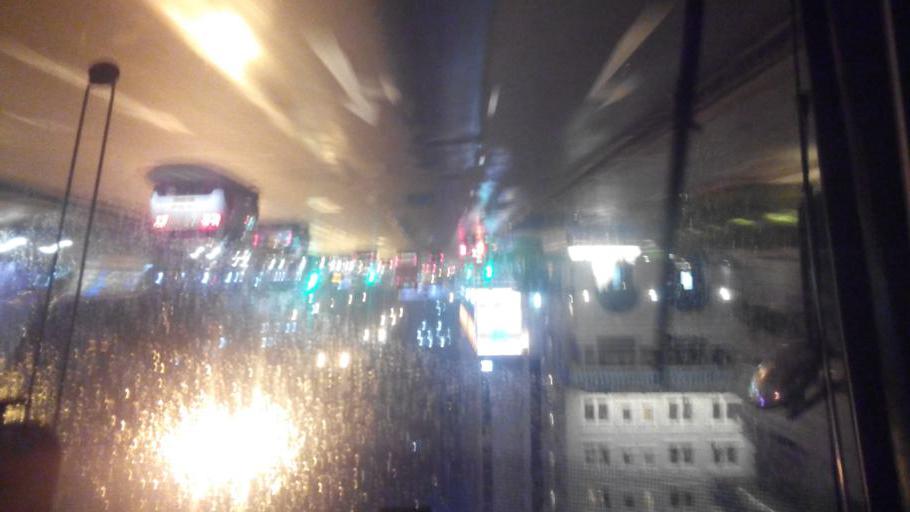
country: HK
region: Wanchai
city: Wan Chai
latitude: 22.2946
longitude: 114.1711
